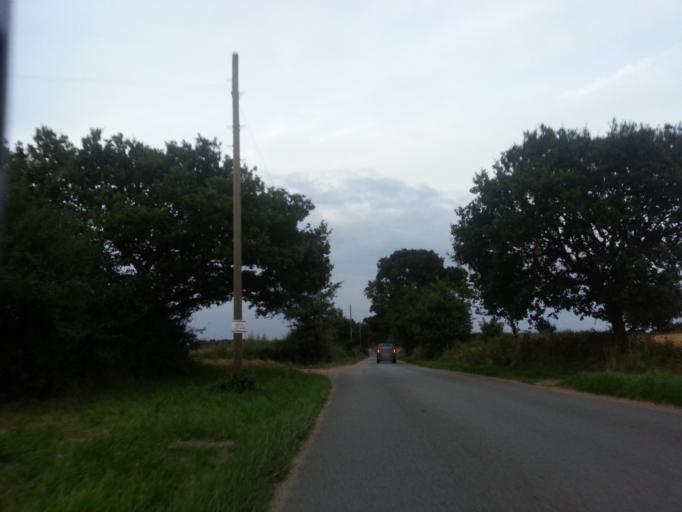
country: GB
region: England
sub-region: Suffolk
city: Kesgrave
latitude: 52.0233
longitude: 1.2110
